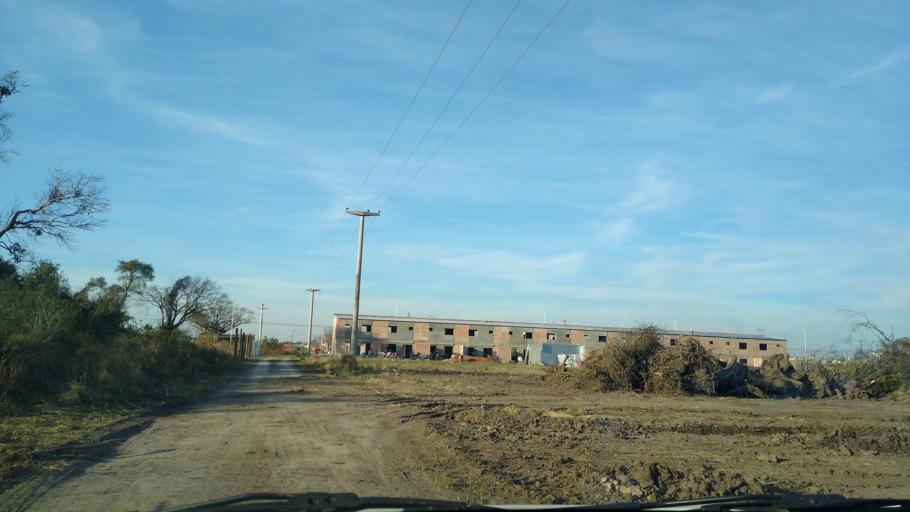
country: AR
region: Chaco
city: Fontana
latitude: -27.4045
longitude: -58.9836
